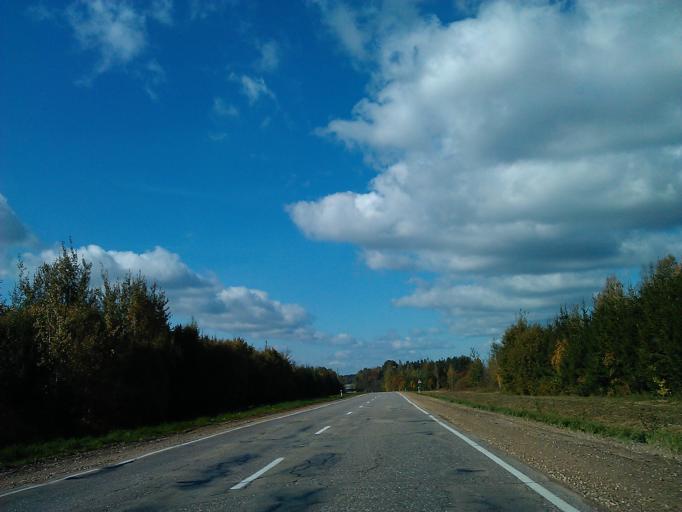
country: LV
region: Livani
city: Livani
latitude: 56.2036
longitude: 26.2741
